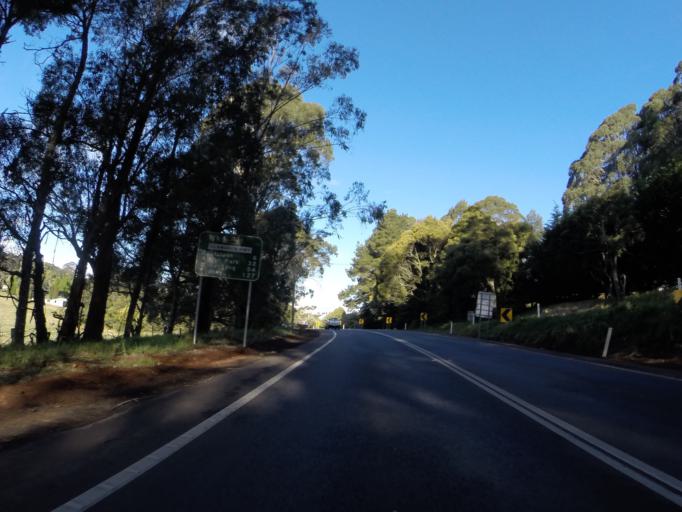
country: AU
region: New South Wales
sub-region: Shoalhaven Shire
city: Kangaroo Valley
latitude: -34.5883
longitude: 150.5440
